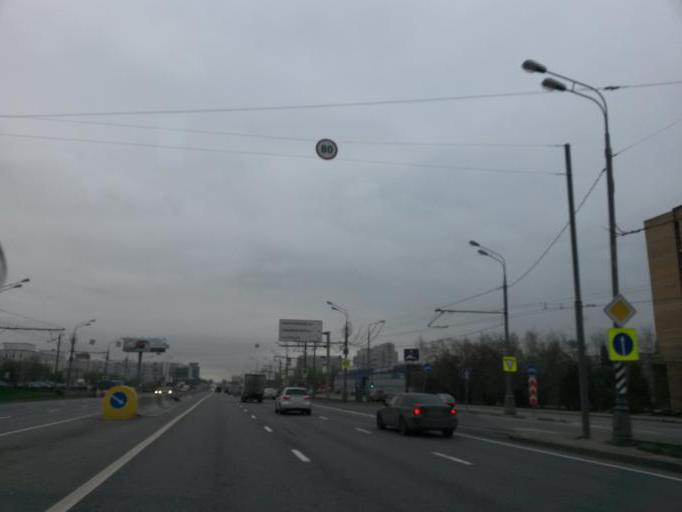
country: RU
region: Moscow
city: Chertanovo Yuzhnoye
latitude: 55.6126
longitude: 37.6102
